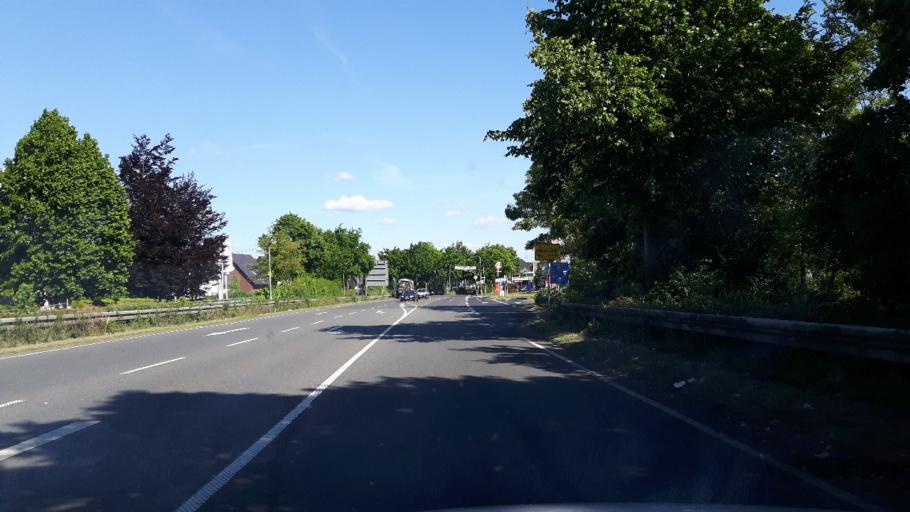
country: DE
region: North Rhine-Westphalia
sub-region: Regierungsbezirk Koln
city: Hennef
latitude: 50.7807
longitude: 7.2701
